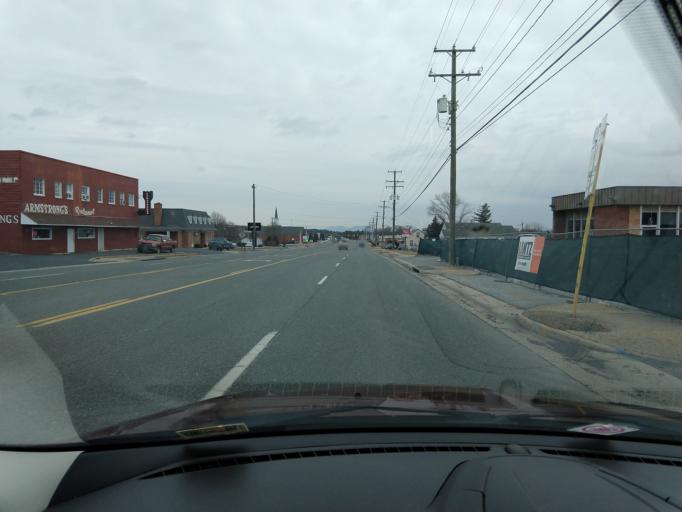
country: US
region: Virginia
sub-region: Augusta County
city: Verona
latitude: 38.1997
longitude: -79.0113
